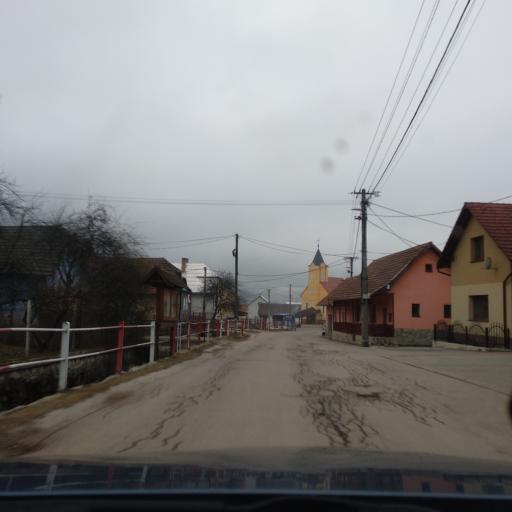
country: SK
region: Nitriansky
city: Ilava
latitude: 48.9118
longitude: 18.2968
